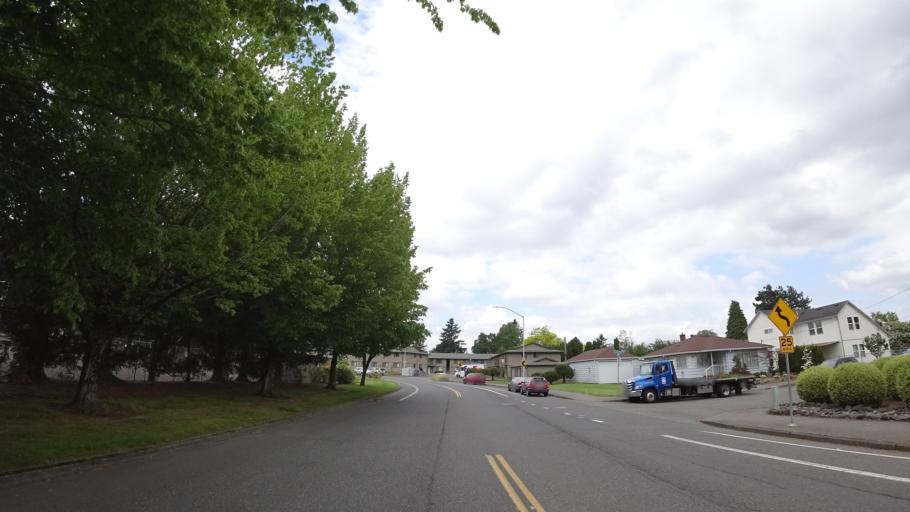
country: US
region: Oregon
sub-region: Multnomah County
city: Lents
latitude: 45.5074
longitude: -122.5635
